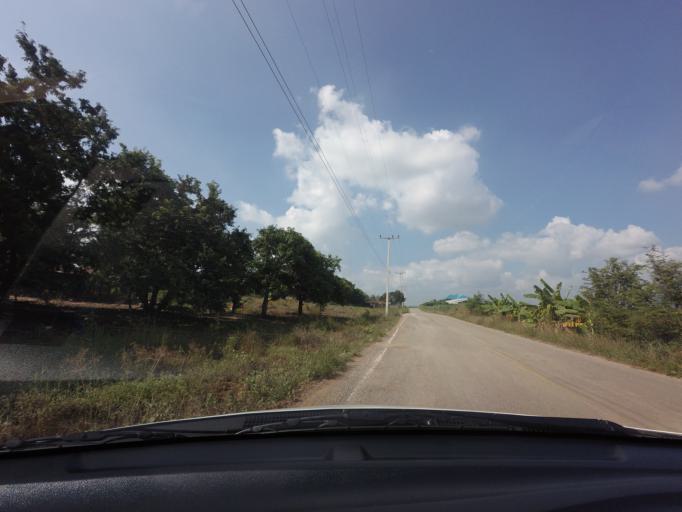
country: TH
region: Nakhon Ratchasima
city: Wang Nam Khiao
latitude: 14.4921
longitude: 101.6268
